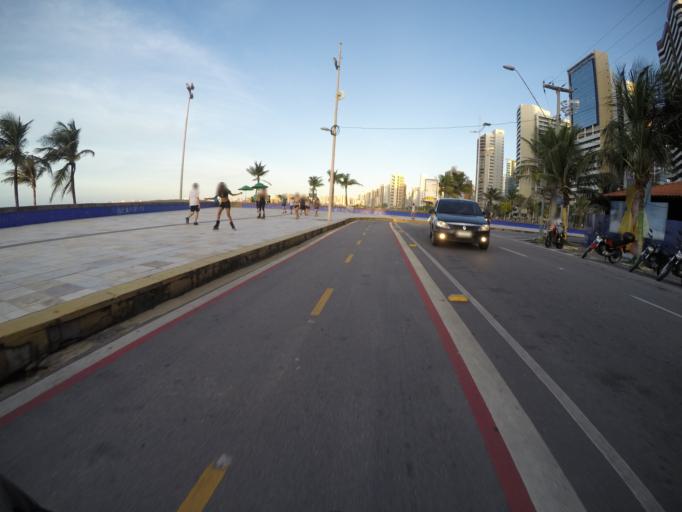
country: BR
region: Ceara
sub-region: Fortaleza
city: Fortaleza
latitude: -3.7210
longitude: -38.5097
